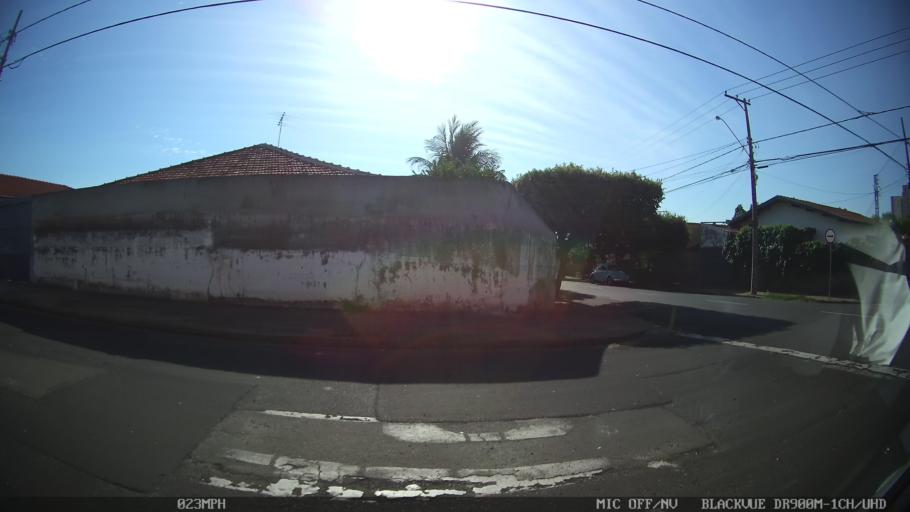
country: BR
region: Sao Paulo
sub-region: Sao Jose Do Rio Preto
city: Sao Jose do Rio Preto
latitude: -20.7985
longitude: -49.3915
